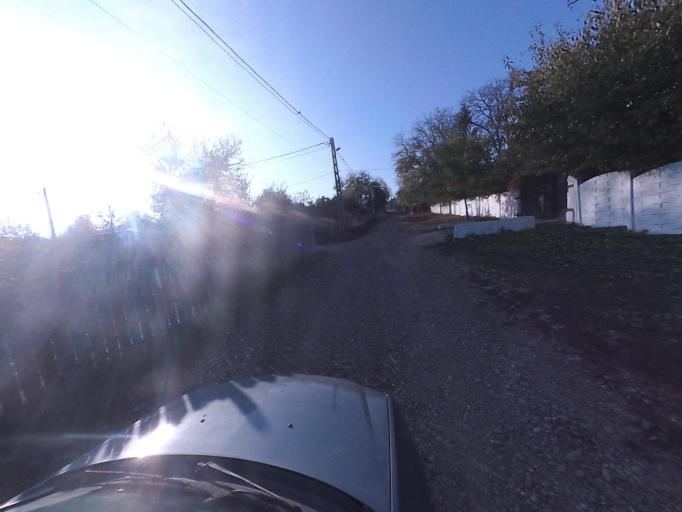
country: RO
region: Vaslui
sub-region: Comuna Bacesti
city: Bacesti
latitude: 46.8233
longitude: 27.2405
